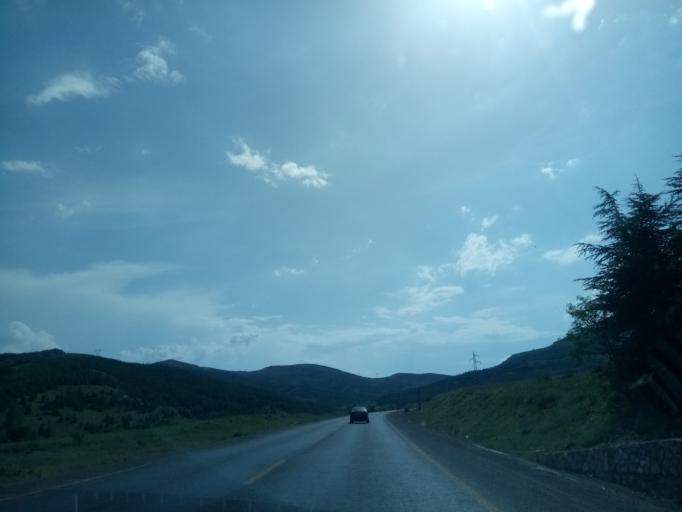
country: TR
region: Isparta
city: Bagkonak
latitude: 38.2548
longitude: 31.3743
